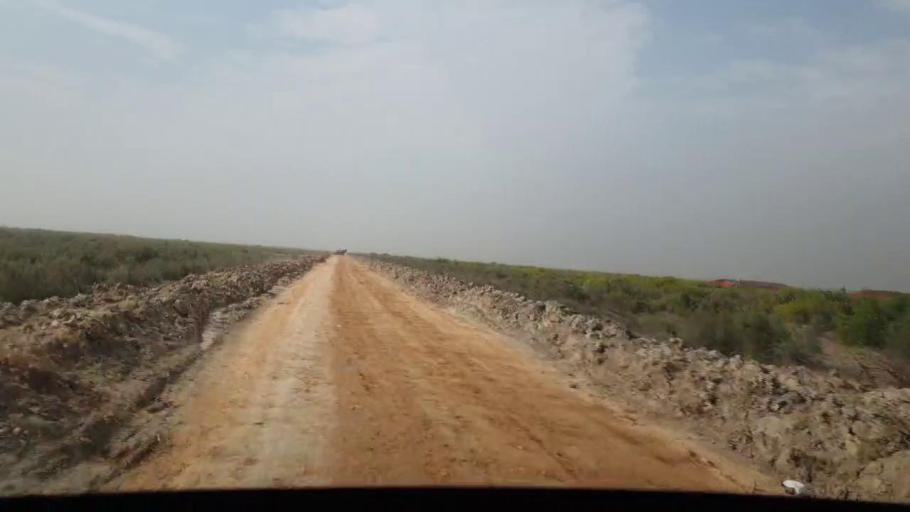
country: PK
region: Sindh
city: Chuhar Jamali
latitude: 24.3535
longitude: 67.9218
